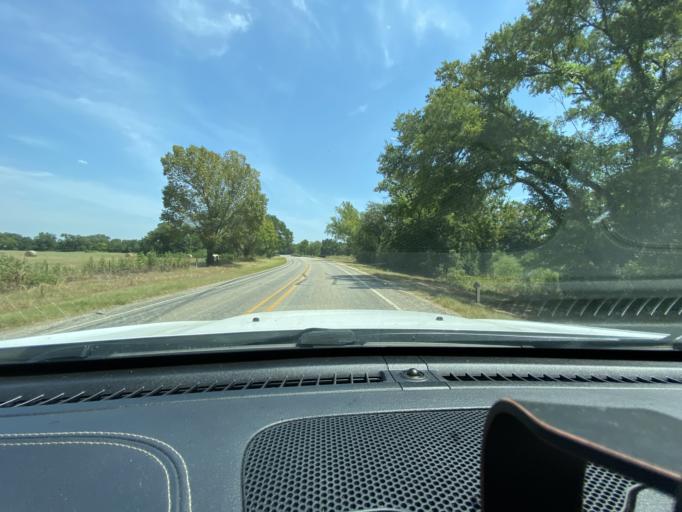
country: US
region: Texas
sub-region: Lee County
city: Giddings
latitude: 30.1510
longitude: -96.9549
